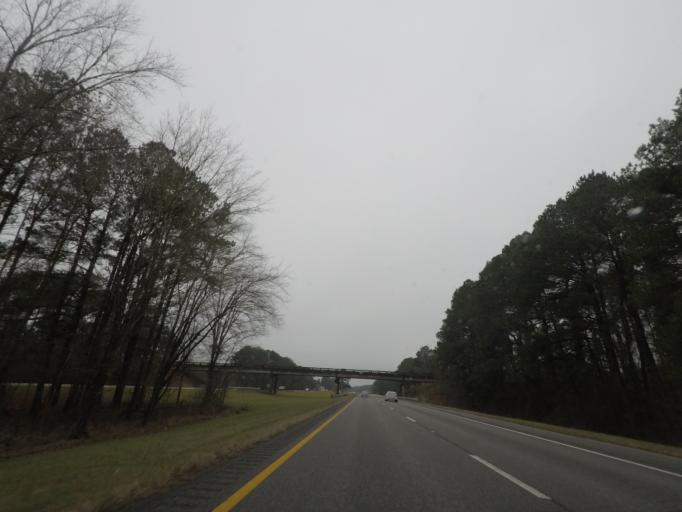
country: US
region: South Carolina
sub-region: Florence County
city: Timmonsville
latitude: 33.9867
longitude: -80.0247
